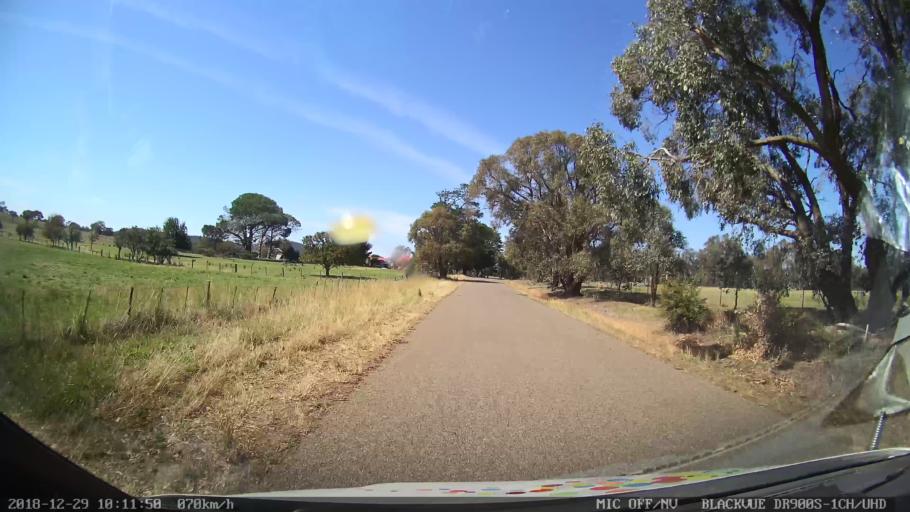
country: AU
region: New South Wales
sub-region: Yass Valley
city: Gundaroo
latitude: -34.8879
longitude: 149.4509
